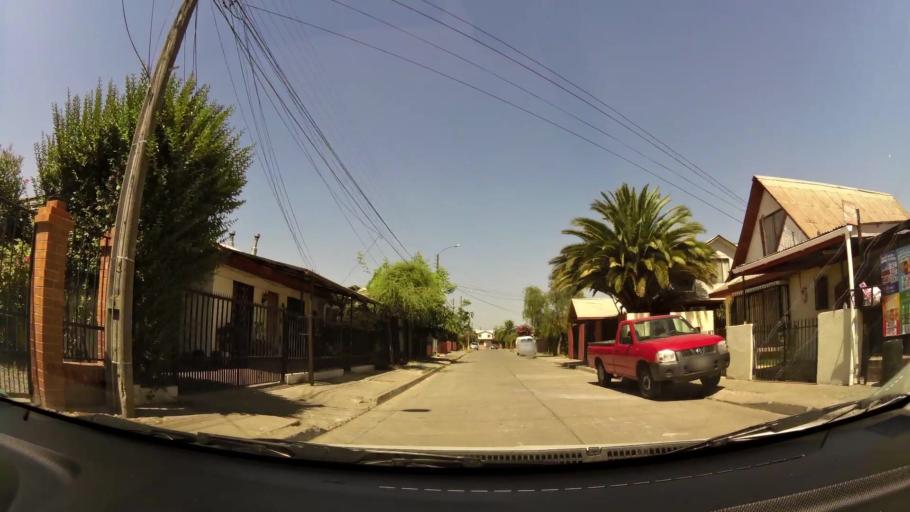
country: CL
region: Maule
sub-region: Provincia de Talca
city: Talca
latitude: -35.4255
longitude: -71.6280
